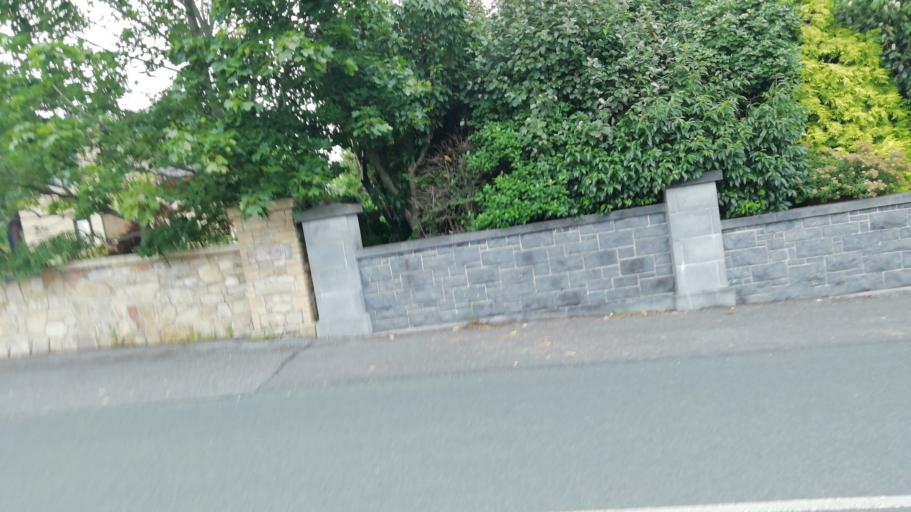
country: IE
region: Munster
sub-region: South Tipperary
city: Cluain Meala
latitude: 52.3504
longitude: -7.6885
